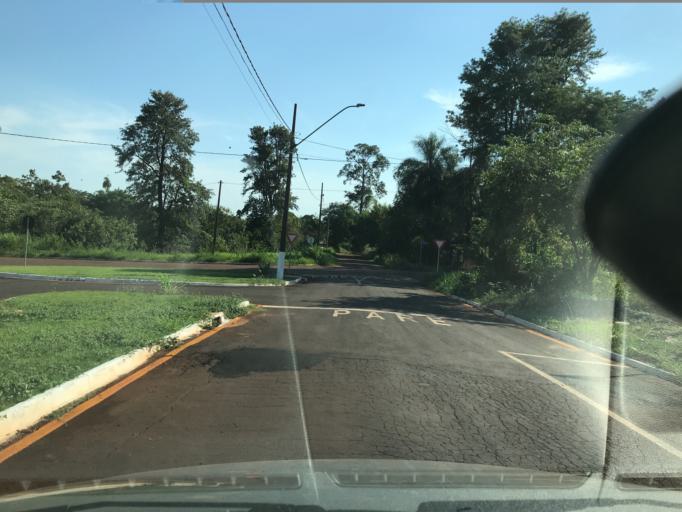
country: BR
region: Parana
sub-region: Palotina
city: Palotina
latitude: -24.2880
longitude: -53.8282
